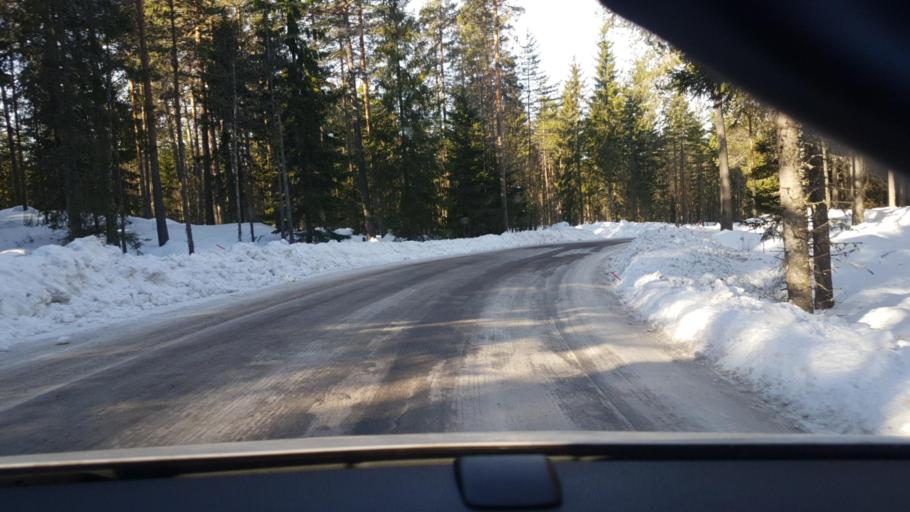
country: NO
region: Hedmark
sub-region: Eidskog
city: Skotterud
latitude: 59.8065
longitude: 12.0870
